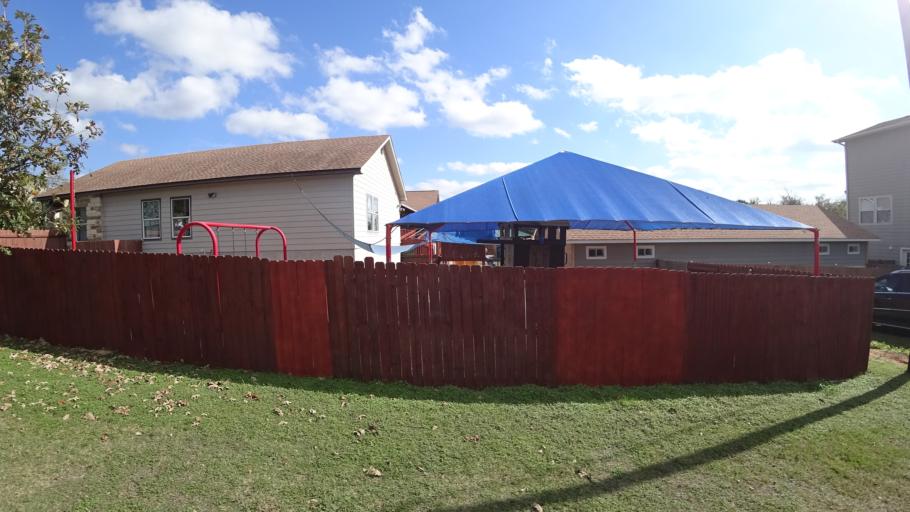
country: US
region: Texas
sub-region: Travis County
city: Barton Creek
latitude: 30.2557
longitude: -97.8937
